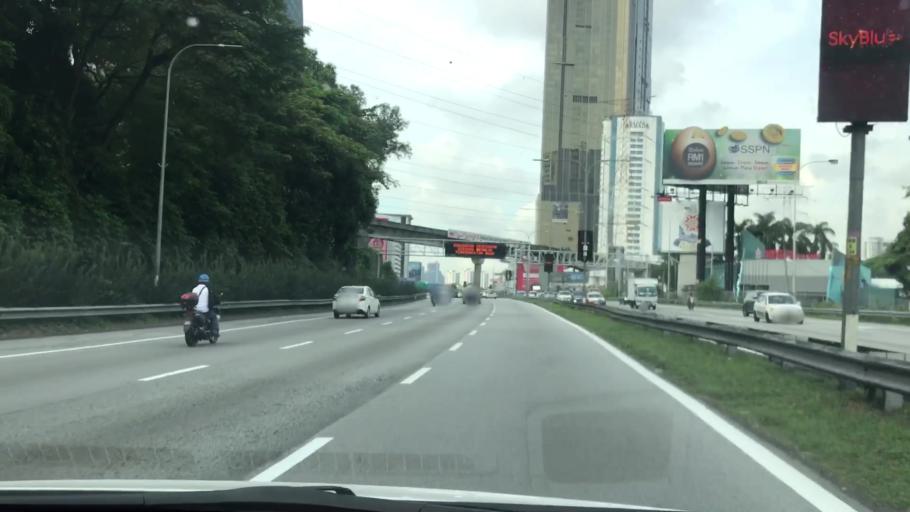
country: MY
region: Selangor
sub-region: Petaling
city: Petaling Jaya
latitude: 3.1056
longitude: 101.6447
